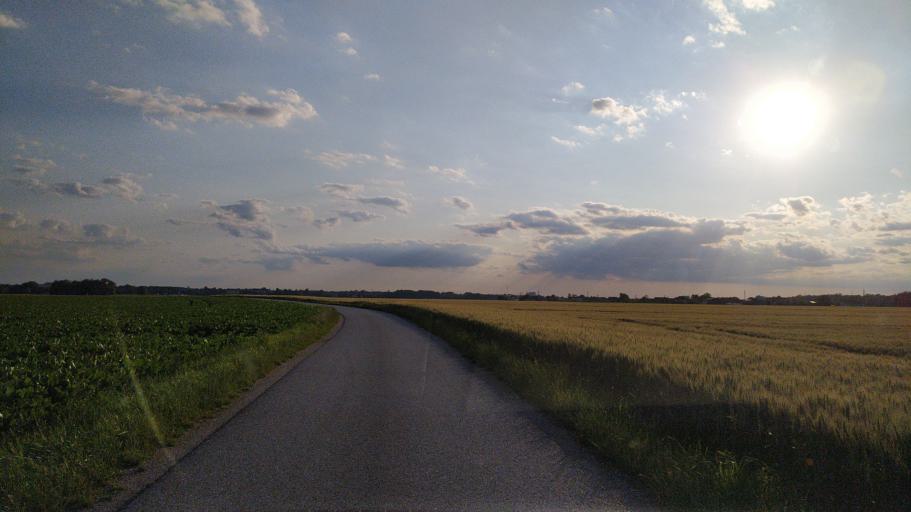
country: AT
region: Lower Austria
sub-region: Politischer Bezirk Amstetten
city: Ennsdorf
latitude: 48.2254
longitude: 14.5592
